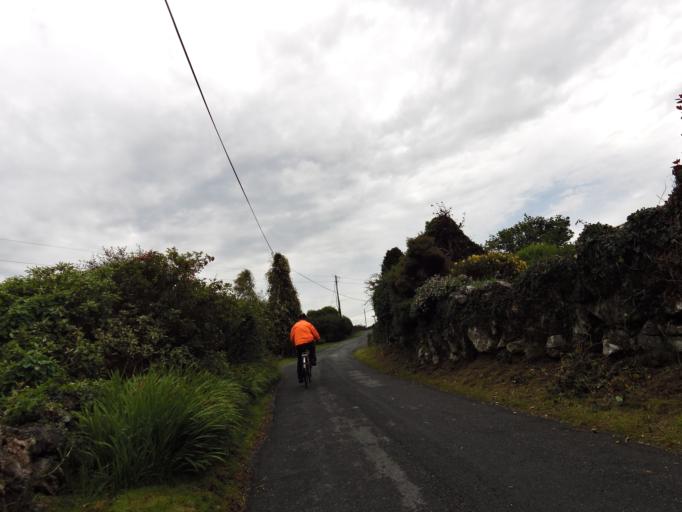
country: IE
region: Connaught
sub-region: County Galway
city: Gaillimh
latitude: 53.3037
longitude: -9.0739
